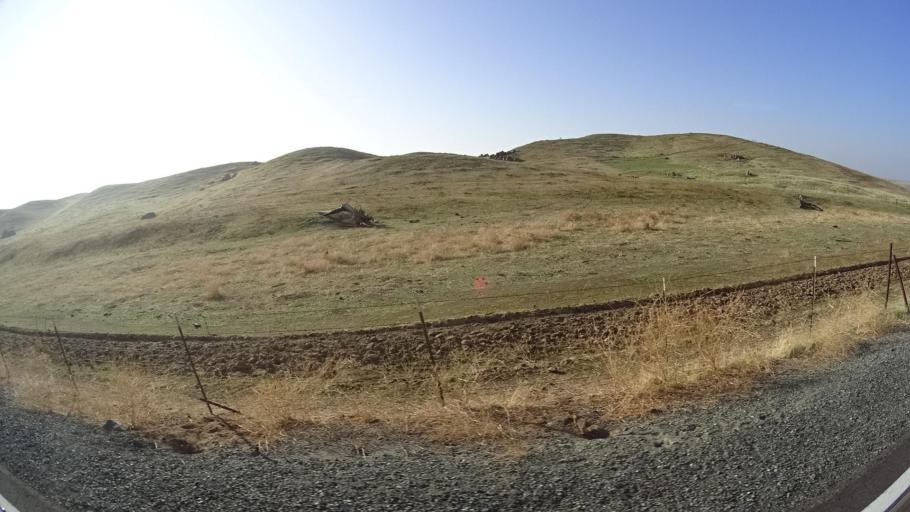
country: US
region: California
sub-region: Tulare County
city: Richgrove
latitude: 35.7417
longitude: -118.9117
